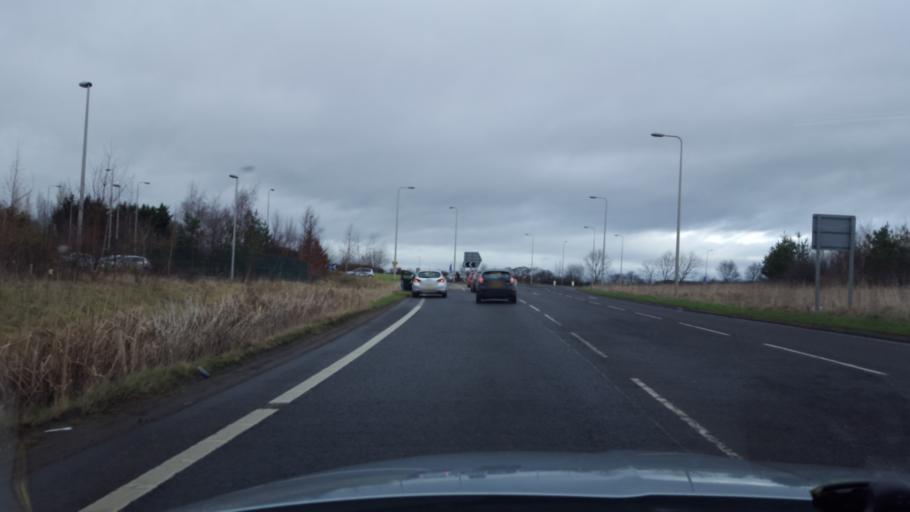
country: GB
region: Scotland
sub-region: Edinburgh
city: Currie
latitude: 55.9171
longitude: -3.3132
